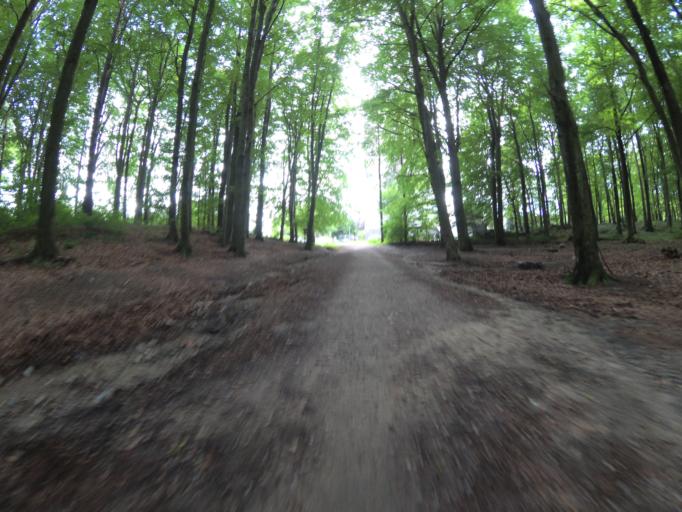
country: PL
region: Pomeranian Voivodeship
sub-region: Gdynia
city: Wielki Kack
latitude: 54.4999
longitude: 18.4947
